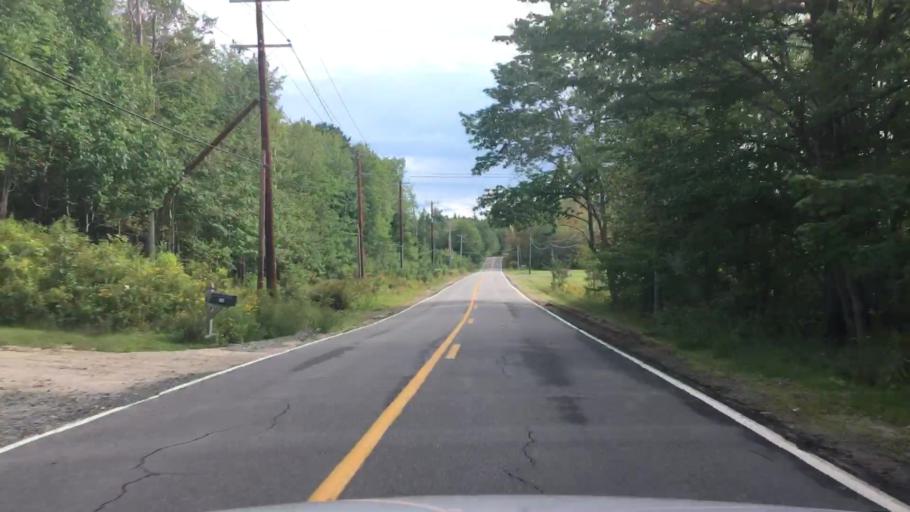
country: US
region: Maine
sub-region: Hancock County
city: Ellsworth
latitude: 44.4867
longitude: -68.4201
